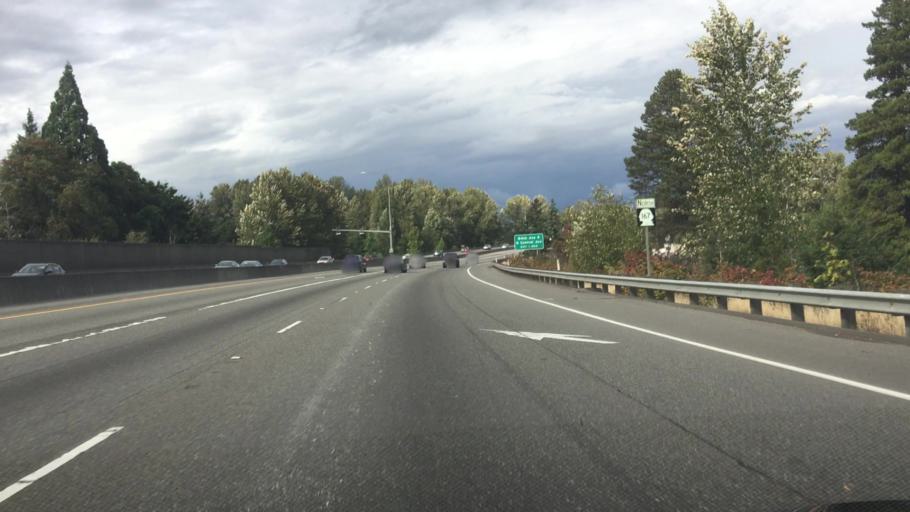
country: US
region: Washington
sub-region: King County
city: Kent
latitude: 47.3842
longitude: -122.2444
